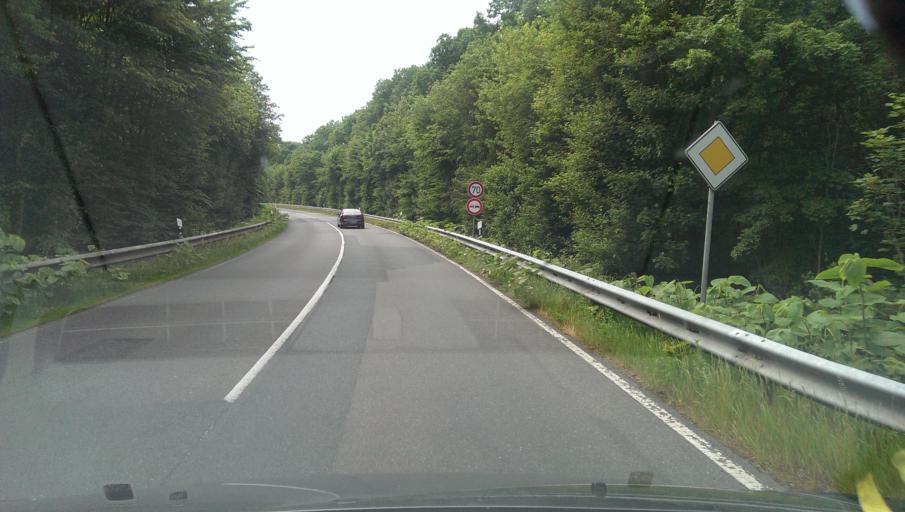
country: DE
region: Lower Saxony
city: Unterluss
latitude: 52.8324
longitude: 10.3021
